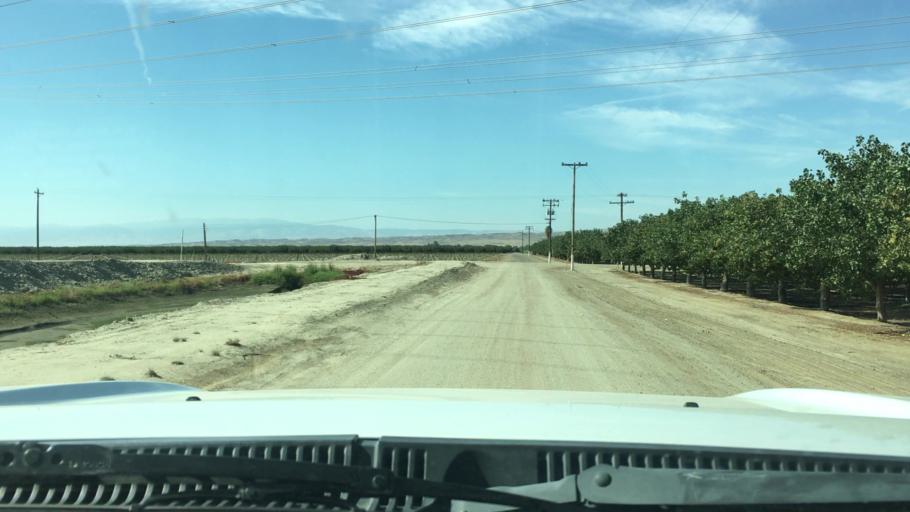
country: US
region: California
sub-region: Kern County
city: Buttonwillow
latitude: 35.3704
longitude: -119.3857
